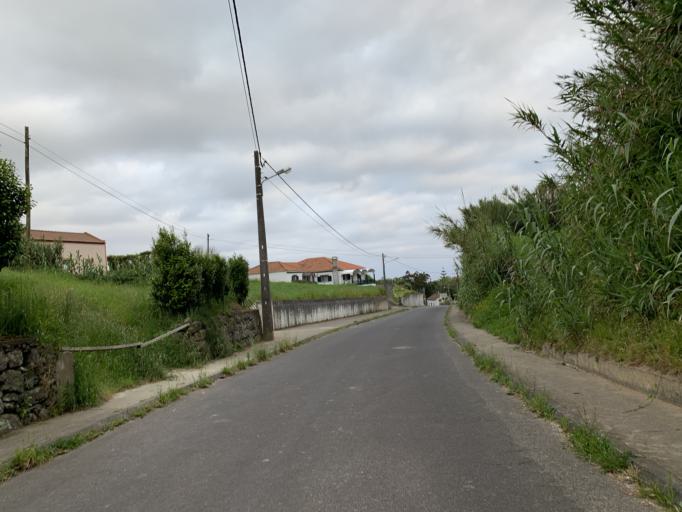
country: PT
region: Azores
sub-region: Ponta Delgada
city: Arrifes
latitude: 37.8463
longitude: -25.8400
